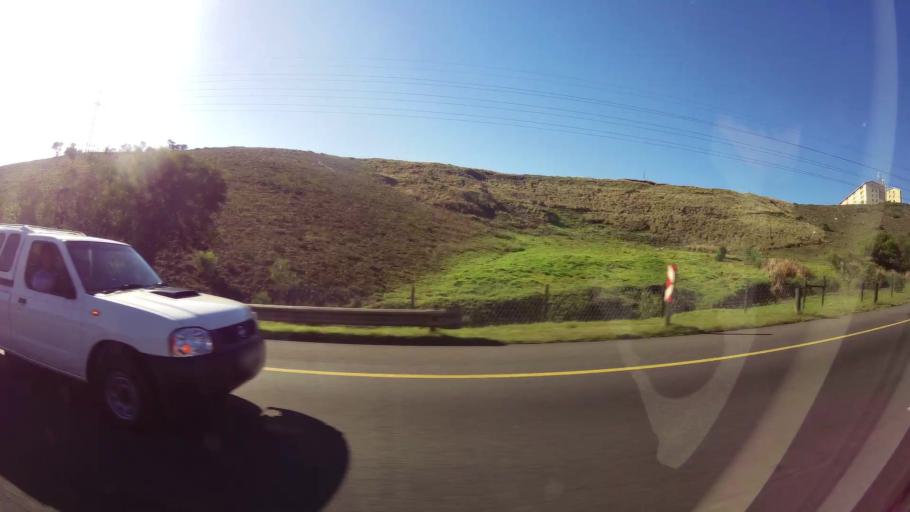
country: ZA
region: Eastern Cape
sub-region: Nelson Mandela Bay Metropolitan Municipality
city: Port Elizabeth
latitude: -33.9325
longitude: 25.5576
